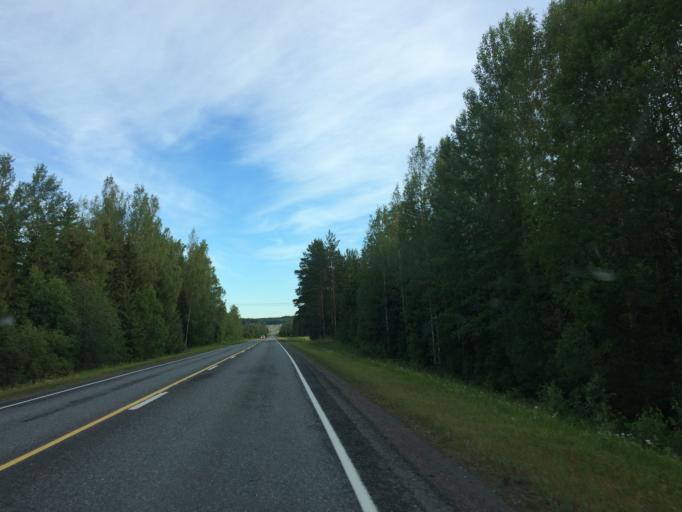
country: FI
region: Haeme
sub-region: Haemeenlinna
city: Janakkala
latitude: 60.8870
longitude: 24.5692
